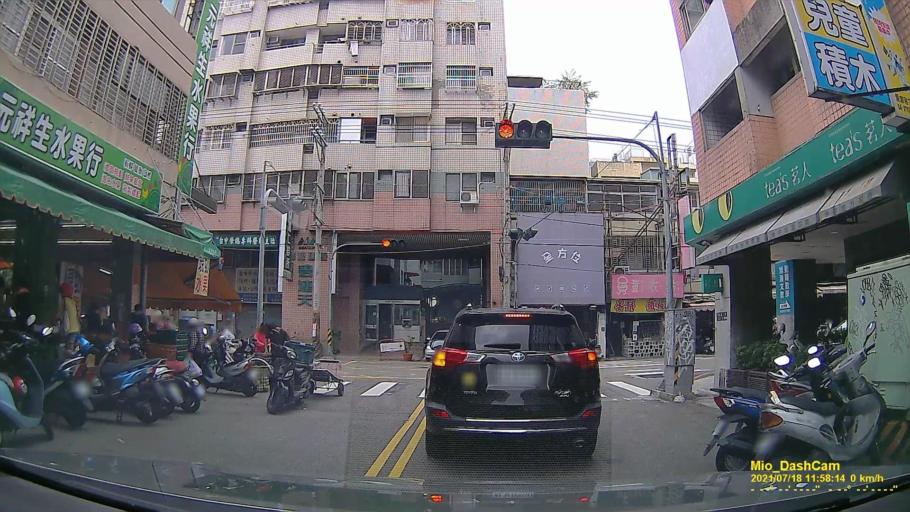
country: TW
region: Taiwan
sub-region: Taichung City
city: Taichung
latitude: 24.1755
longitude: 120.6047
